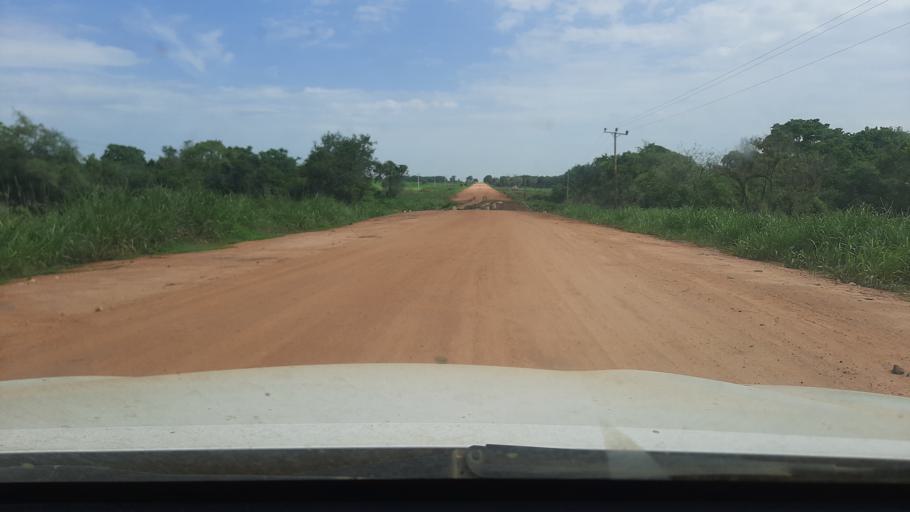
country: ET
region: Gambela
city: Gambela
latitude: 8.0198
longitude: 34.5732
